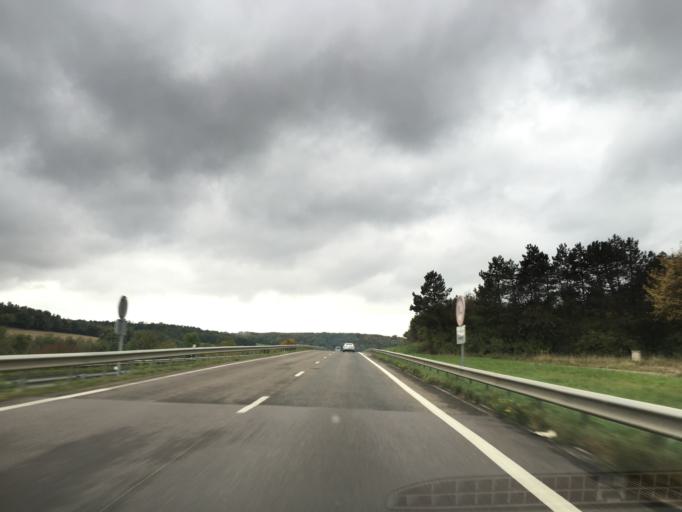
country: FR
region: Lorraine
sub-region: Departement de la Meuse
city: Vacon
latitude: 48.6893
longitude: 5.6084
